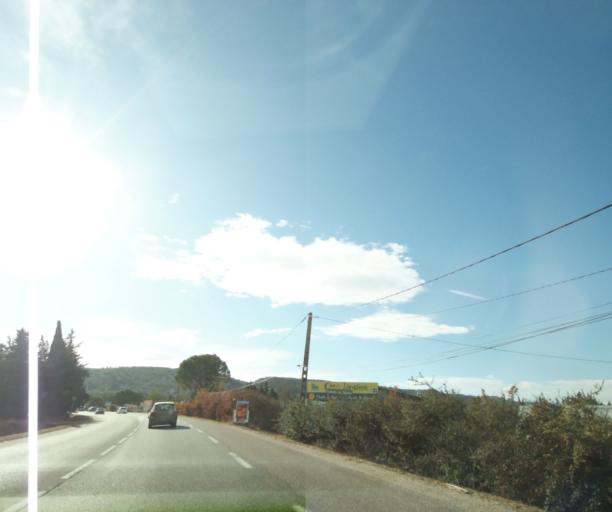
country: FR
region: Provence-Alpes-Cote d'Azur
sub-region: Departement des Bouches-du-Rhone
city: Chateauneuf-les-Martigues
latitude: 43.3787
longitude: 5.1881
